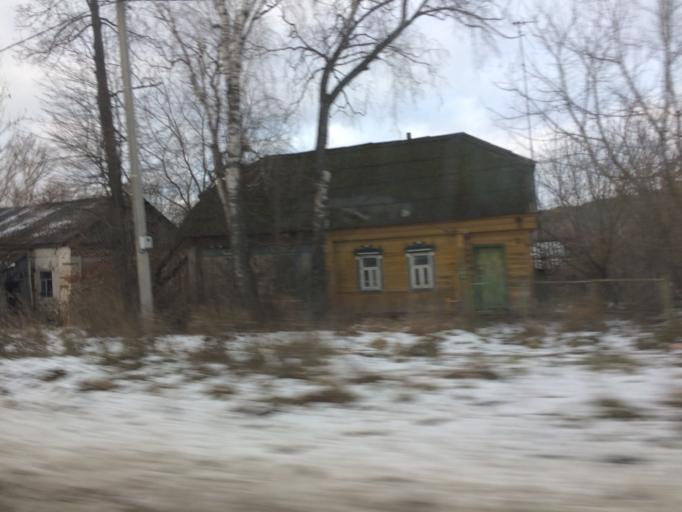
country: RU
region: Tula
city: Cherepet'
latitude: 54.1189
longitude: 36.3817
